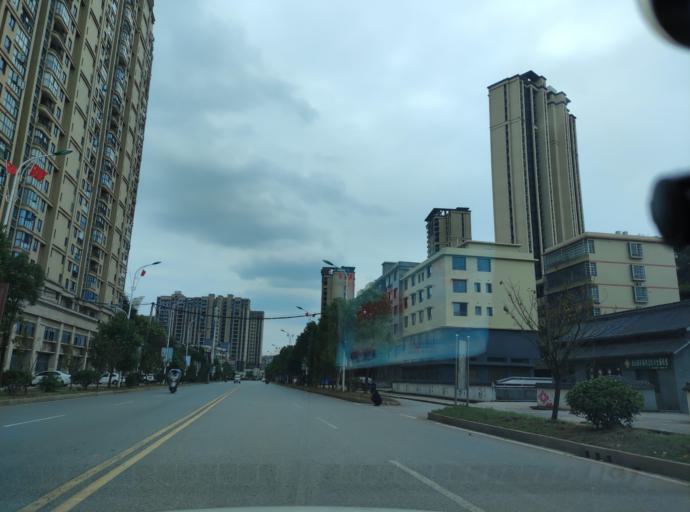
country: CN
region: Jiangxi Sheng
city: Pingxiang
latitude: 27.6793
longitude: 113.9086
